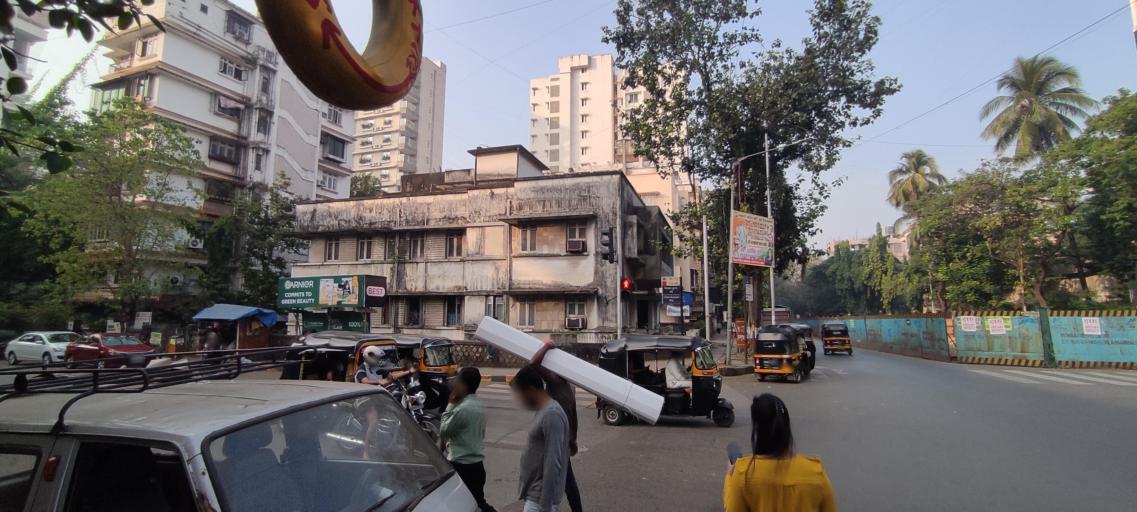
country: IN
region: Maharashtra
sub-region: Mumbai Suburban
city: Mumbai
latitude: 19.0712
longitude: 72.8374
